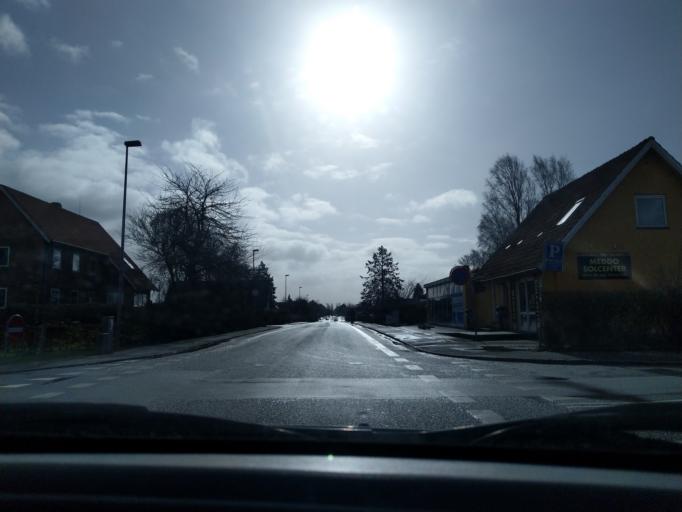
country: DK
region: Zealand
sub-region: Naestved Kommune
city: Naestved
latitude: 55.2186
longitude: 11.7675
